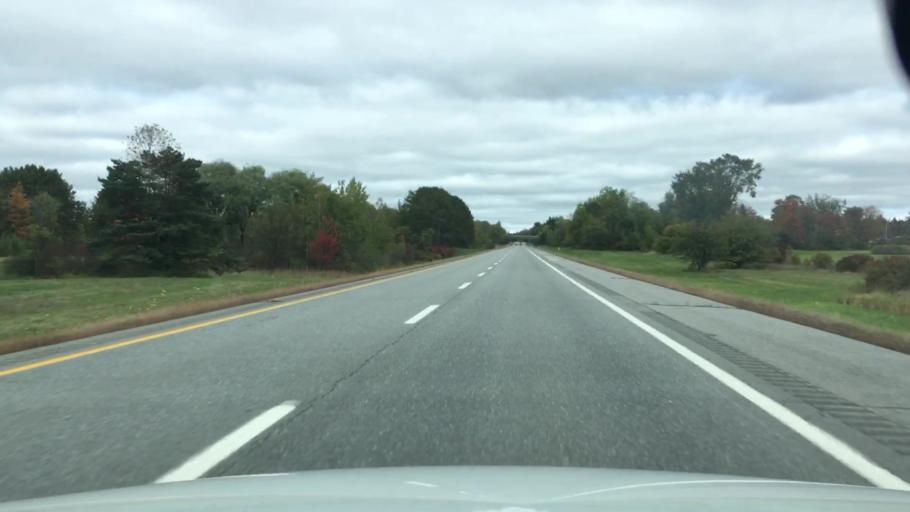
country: US
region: Maine
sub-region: Kennebec County
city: Clinton
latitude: 44.6570
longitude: -69.5046
